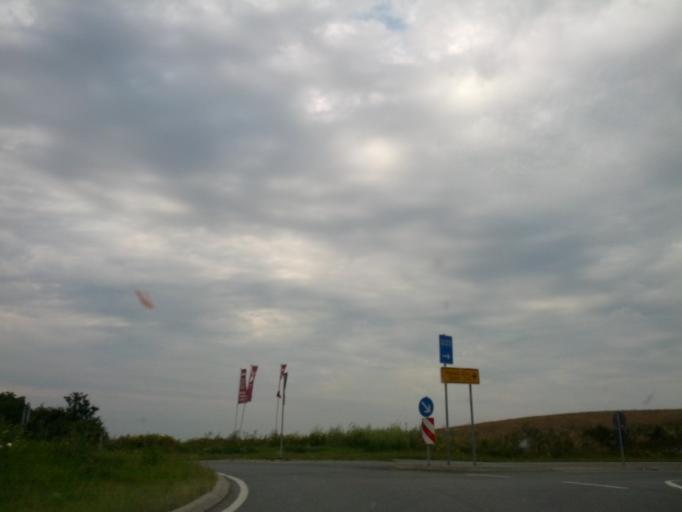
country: DE
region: Mecklenburg-Vorpommern
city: Satow-Oberhagen
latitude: 53.9751
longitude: 11.8669
